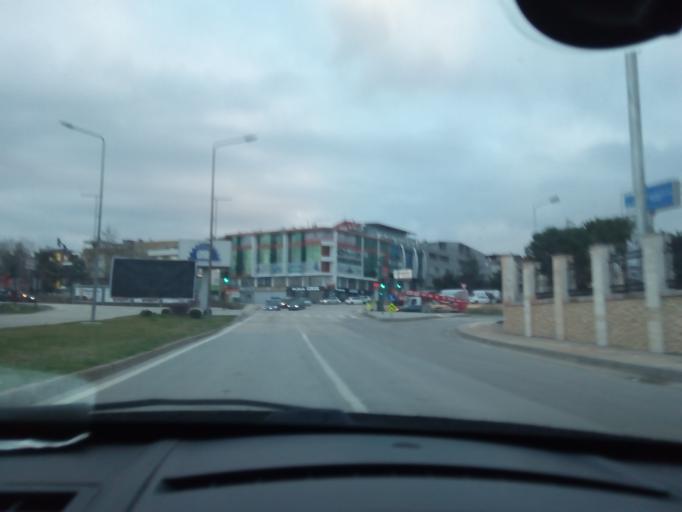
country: TR
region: Bursa
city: Niluefer
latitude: 40.2339
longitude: 28.9688
